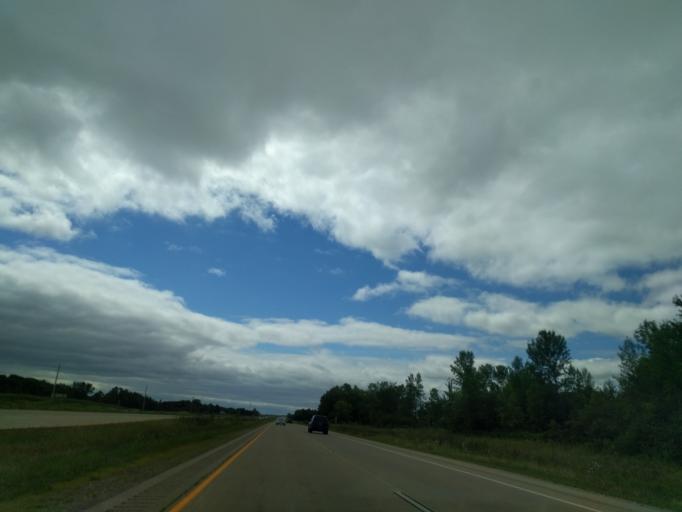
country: US
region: Wisconsin
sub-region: Oconto County
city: Oconto
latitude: 44.9604
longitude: -87.8719
